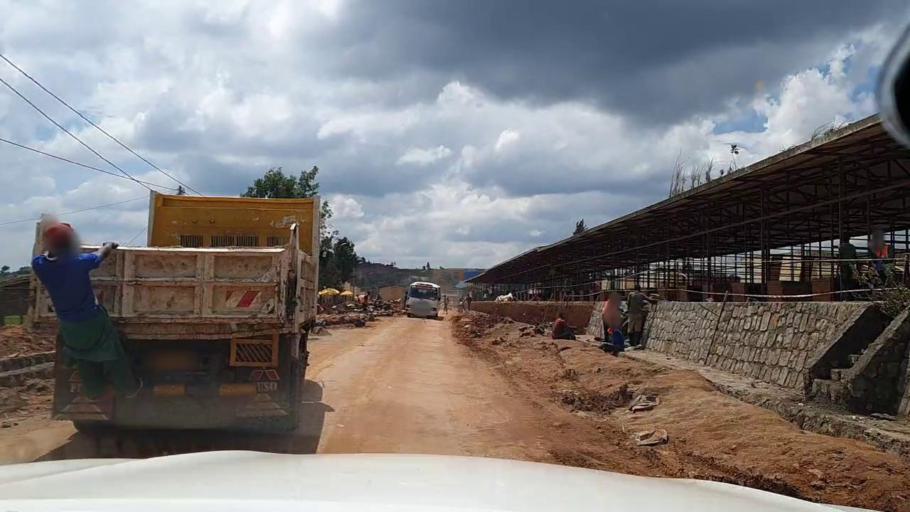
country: RW
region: Southern Province
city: Butare
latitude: -2.6950
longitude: 29.5694
